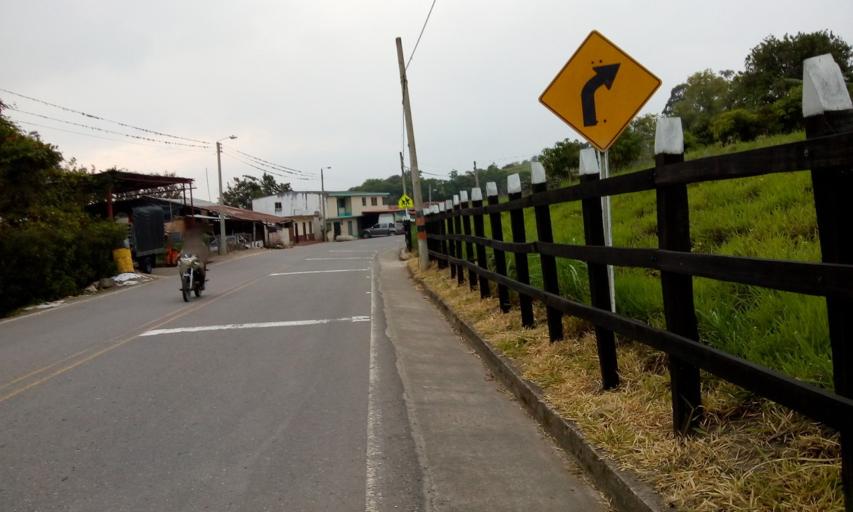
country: CO
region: Boyaca
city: Tipacoque
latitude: 6.4152
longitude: -72.6900
